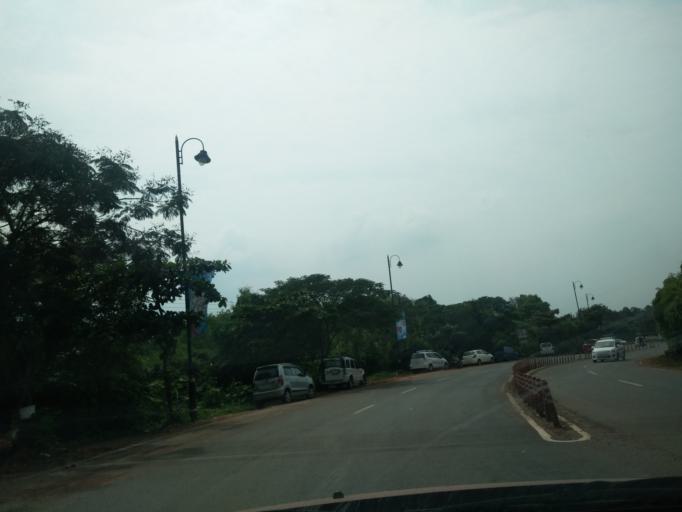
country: IN
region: Goa
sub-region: North Goa
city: Panaji
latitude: 15.4964
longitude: 73.8391
